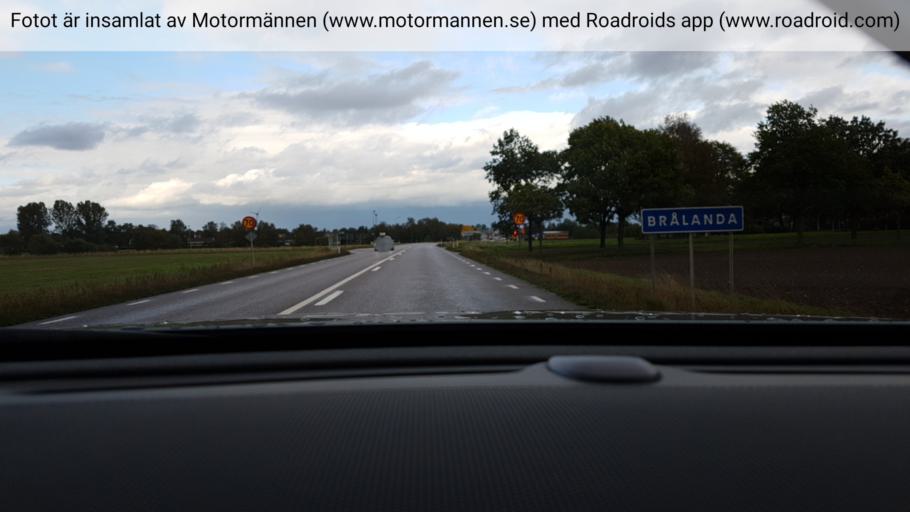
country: SE
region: Vaestra Goetaland
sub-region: Vanersborgs Kommun
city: Bralanda
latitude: 58.5537
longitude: 12.3515
